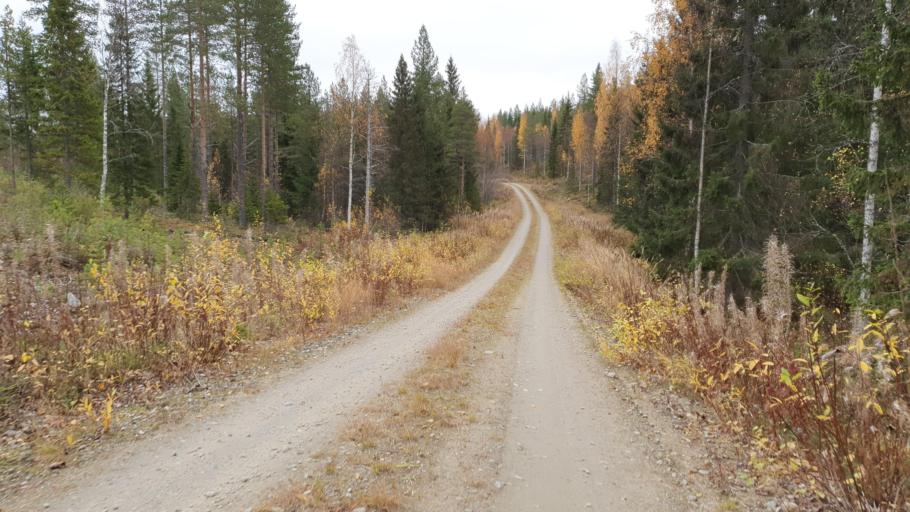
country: FI
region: Kainuu
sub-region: Kehys-Kainuu
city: Kuhmo
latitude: 64.4465
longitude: 29.6216
